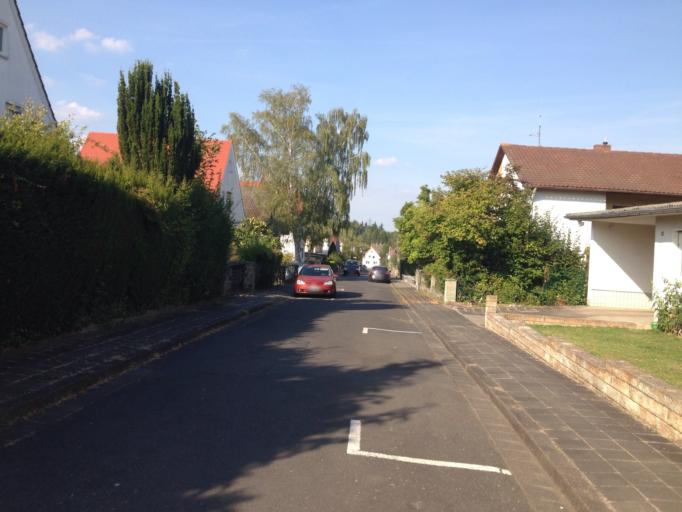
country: DE
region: Hesse
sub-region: Regierungsbezirk Giessen
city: Heuchelheim
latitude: 50.5584
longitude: 8.6504
